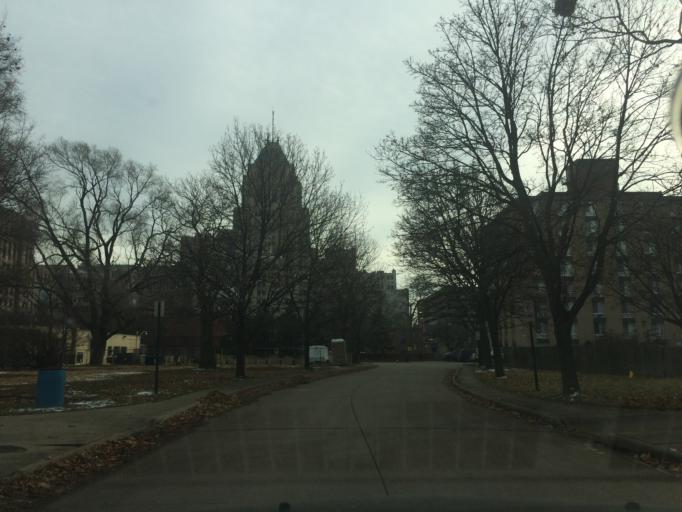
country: US
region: Michigan
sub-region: Wayne County
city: Hamtramck
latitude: 42.3720
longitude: -83.0793
